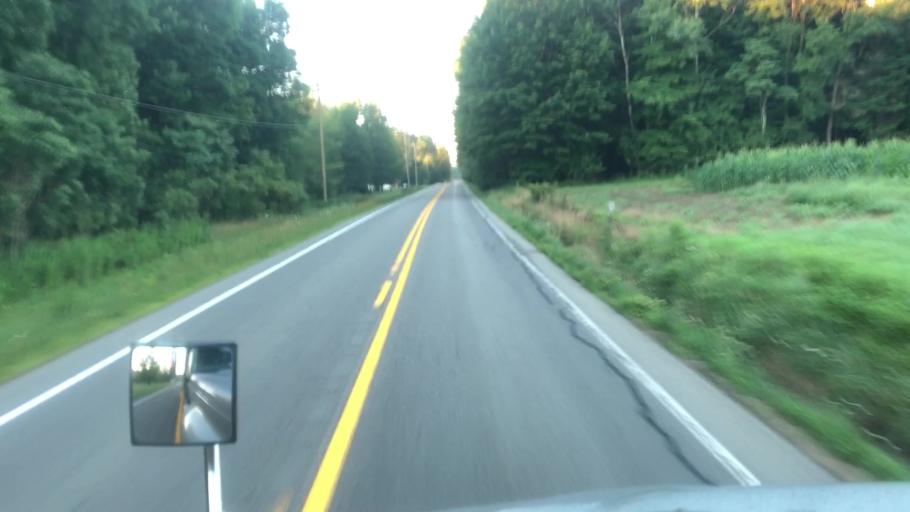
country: US
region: Pennsylvania
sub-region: Crawford County
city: Titusville
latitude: 41.5810
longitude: -79.6097
